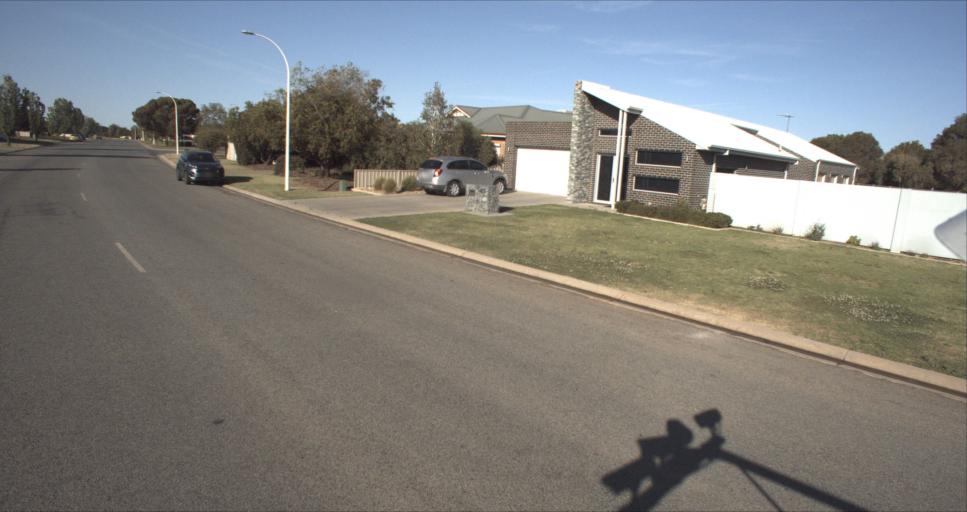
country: AU
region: New South Wales
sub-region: Leeton
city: Leeton
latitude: -34.5415
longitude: 146.4004
